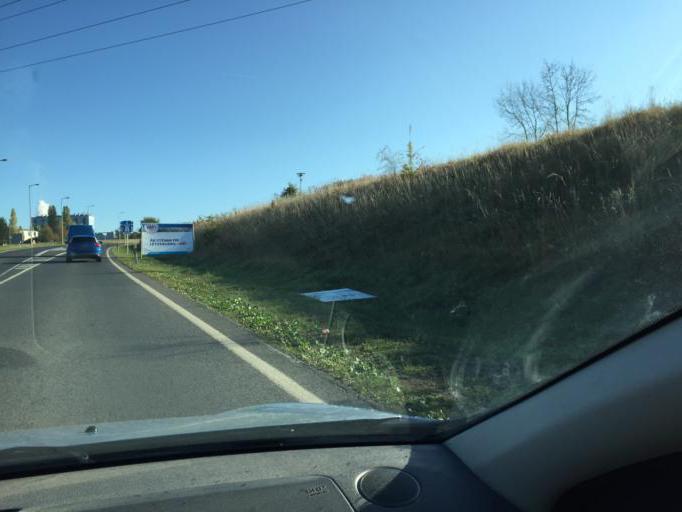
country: LU
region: Luxembourg
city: Colmar
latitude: 49.8014
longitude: 6.1000
